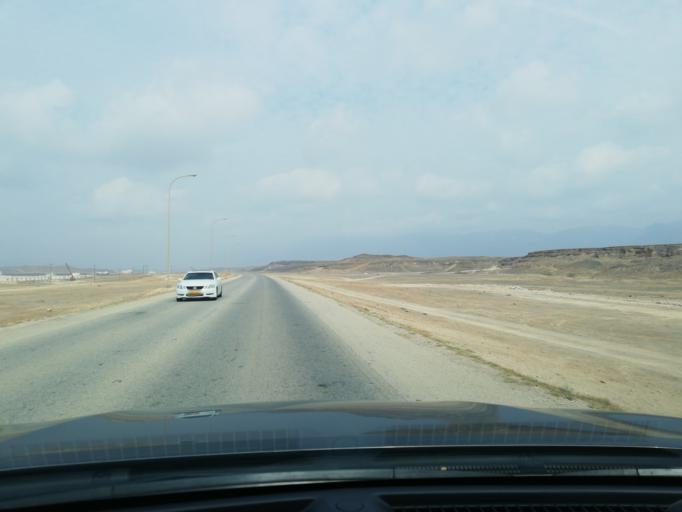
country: OM
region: Zufar
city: Salalah
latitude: 16.9553
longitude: 53.9140
